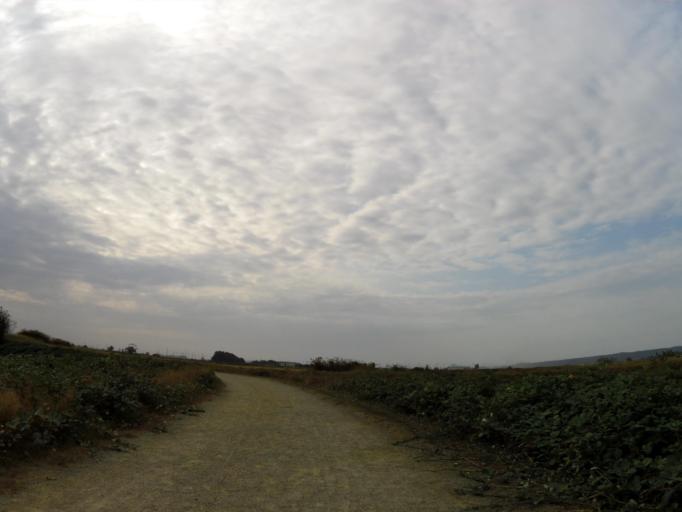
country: US
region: Washington
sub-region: Skagit County
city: Mount Vernon
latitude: 48.4586
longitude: -122.4721
